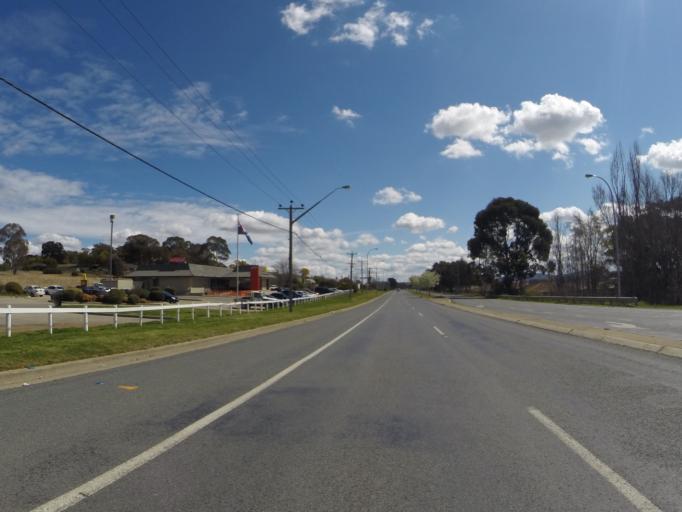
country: AU
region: New South Wales
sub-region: Goulburn Mulwaree
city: Goulburn
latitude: -34.7475
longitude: 149.7487
